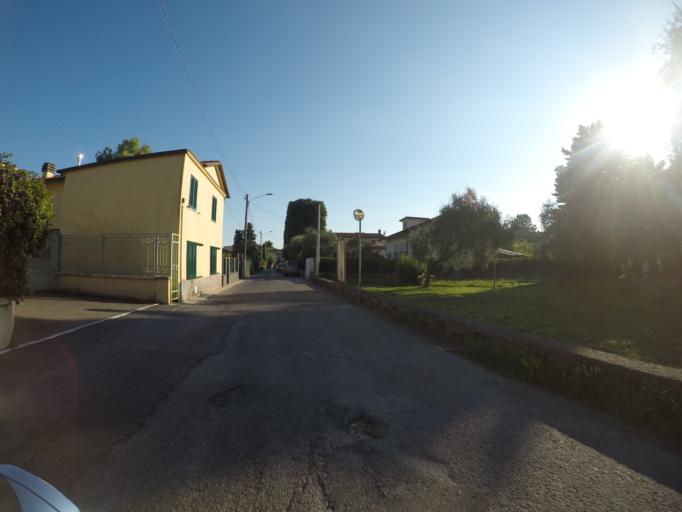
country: IT
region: Tuscany
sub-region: Provincia di Massa-Carrara
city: Massa
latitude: 44.0307
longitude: 10.1363
